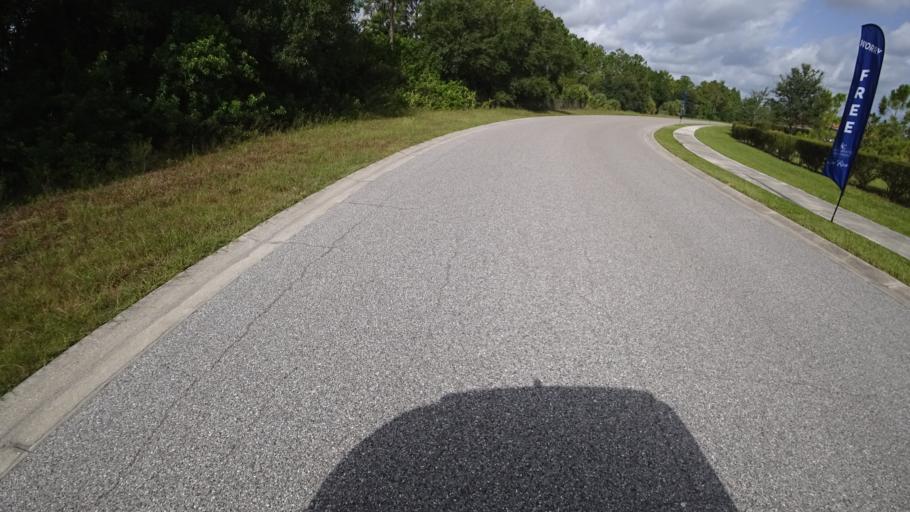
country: US
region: Florida
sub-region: Sarasota County
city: Desoto Lakes
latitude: 27.4389
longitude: -82.4626
